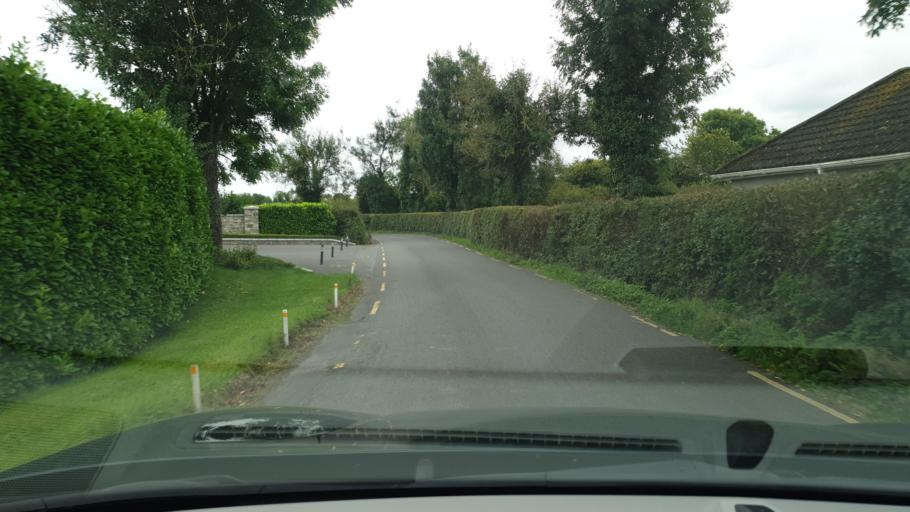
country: IE
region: Leinster
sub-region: Kildare
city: Clane
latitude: 53.3005
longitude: -6.7125
